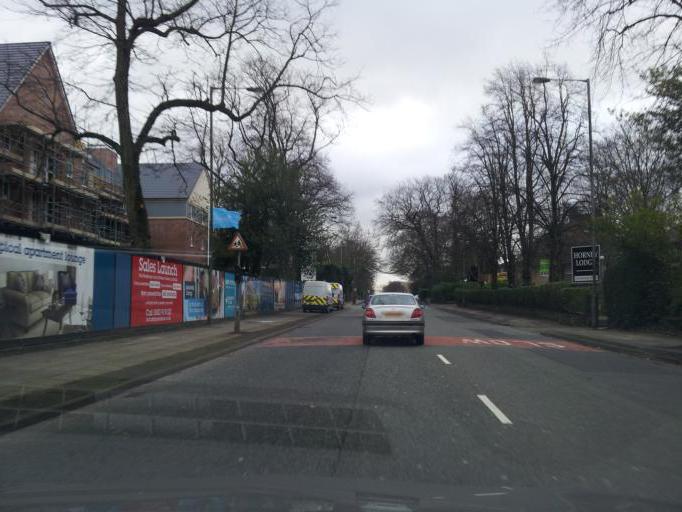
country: GB
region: England
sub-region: Borough of Bury
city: Prestwich
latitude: 53.5268
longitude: -2.2794
